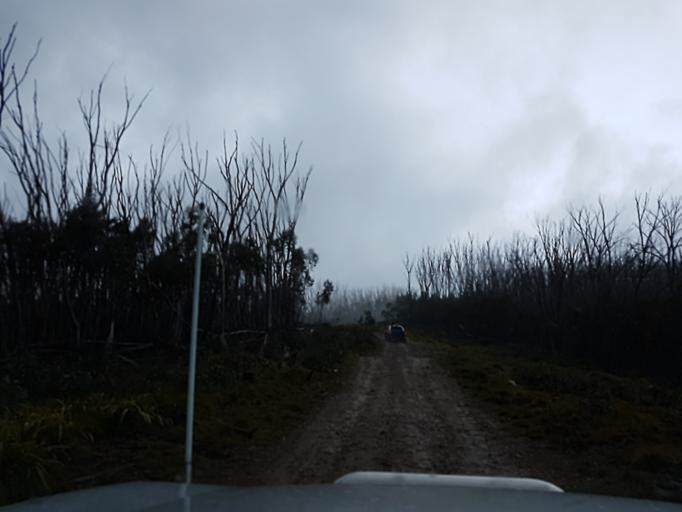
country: AU
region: Victoria
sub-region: Alpine
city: Mount Beauty
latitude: -37.0898
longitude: 147.0994
